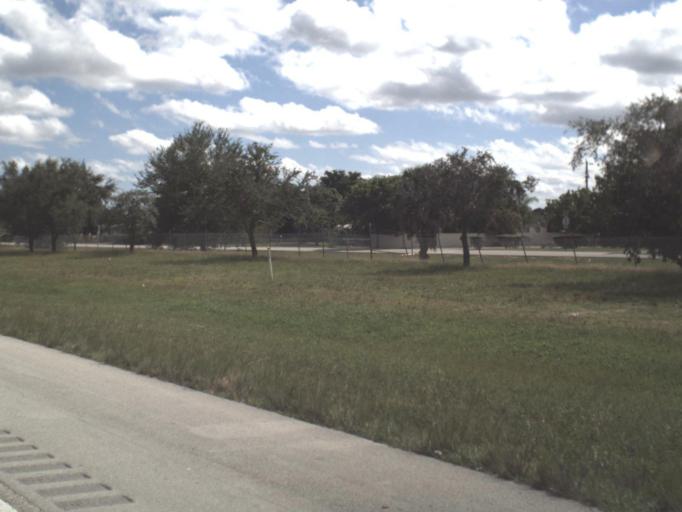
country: US
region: Florida
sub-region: Miami-Dade County
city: Lake Lucerne
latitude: 25.9719
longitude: -80.2571
